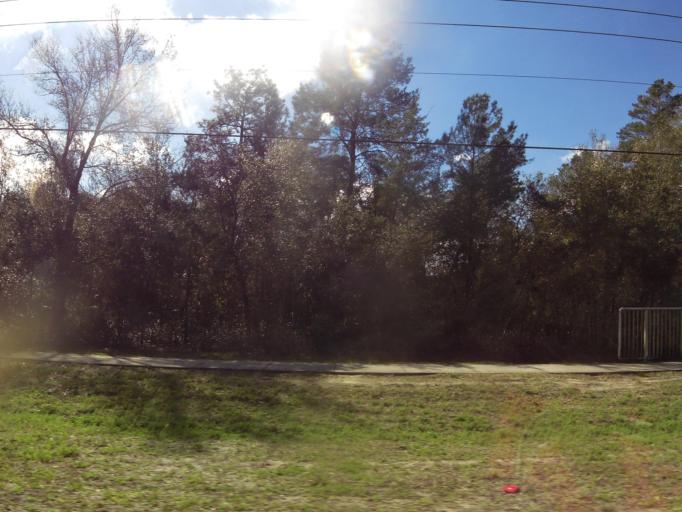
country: US
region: Florida
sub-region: Volusia County
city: Orange City
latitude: 28.9342
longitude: -81.3059
